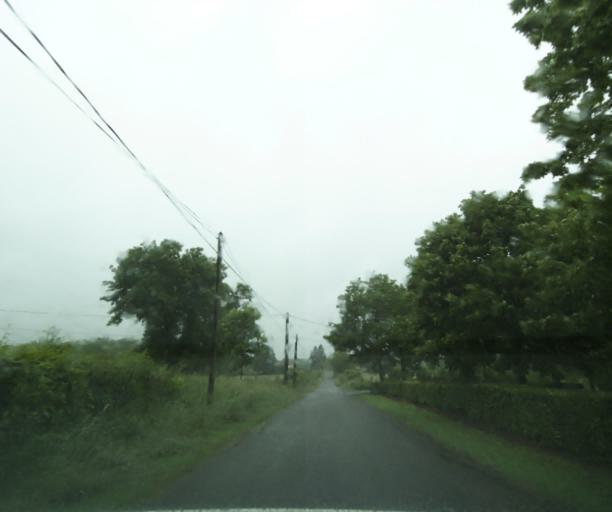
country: FR
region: Bourgogne
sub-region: Departement de Saone-et-Loire
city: Ciry-le-Noble
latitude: 46.5722
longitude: 4.3325
